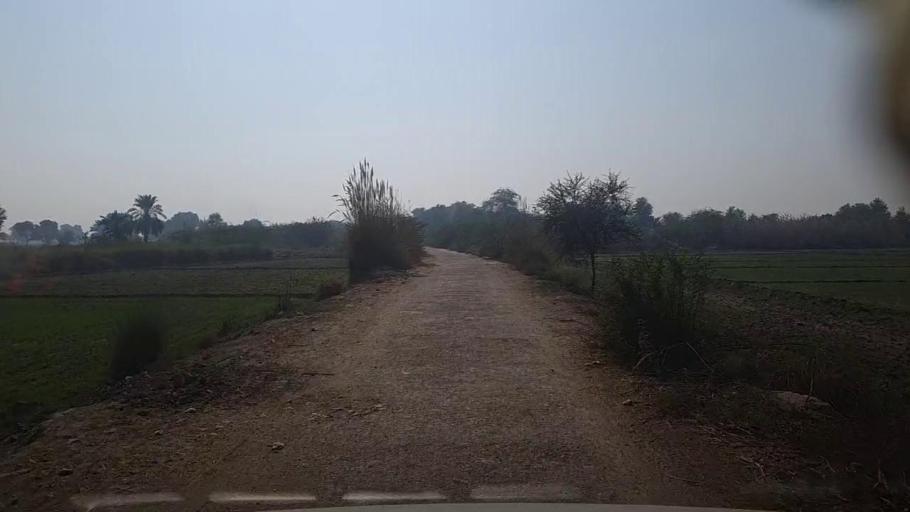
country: PK
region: Sindh
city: Kandiari
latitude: 26.9796
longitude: 68.4694
